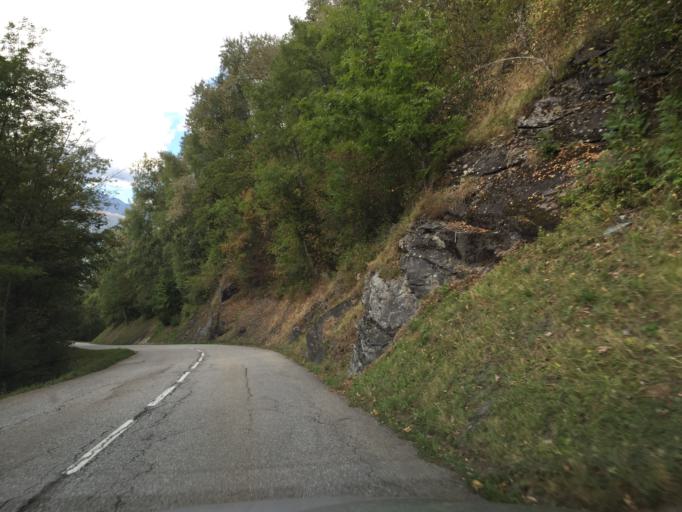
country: FR
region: Rhone-Alpes
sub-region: Departement de la Savoie
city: Bourg-Saint-Maurice
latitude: 45.5625
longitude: 6.7507
